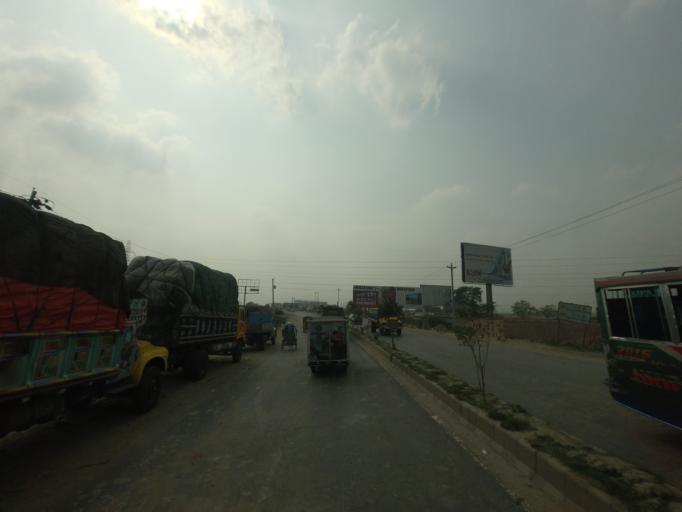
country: BD
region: Dhaka
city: Azimpur
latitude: 23.7900
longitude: 90.3236
